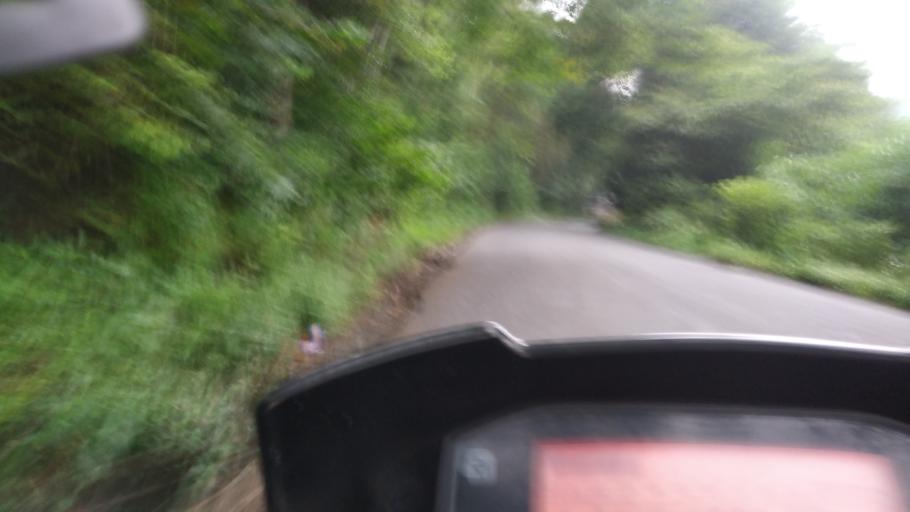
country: IN
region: Kerala
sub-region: Idukki
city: Kuttampuzha
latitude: 10.0649
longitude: 76.7883
